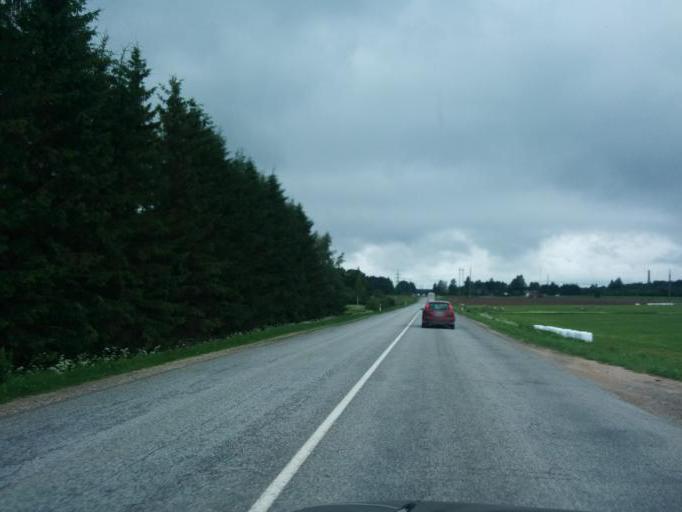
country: LV
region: Beverina
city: Murmuiza
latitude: 57.5083
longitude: 25.4593
